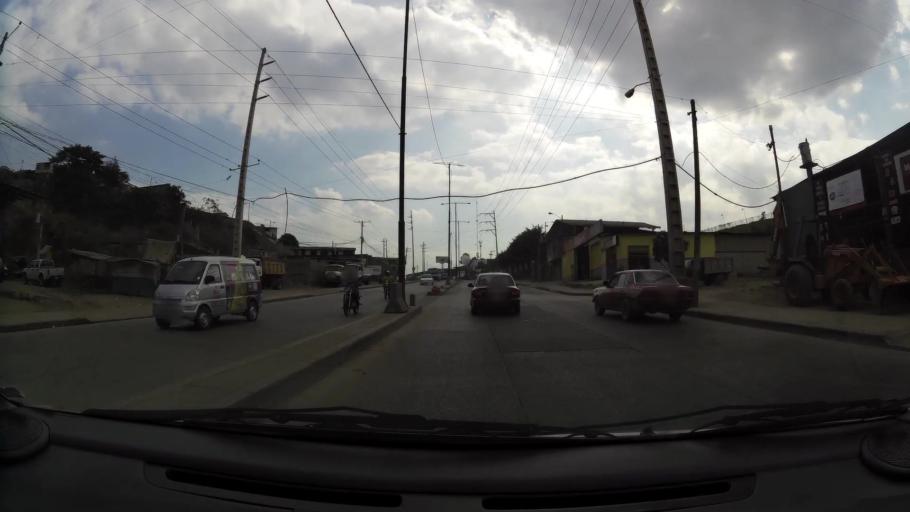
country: EC
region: Guayas
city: Santa Lucia
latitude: -2.1183
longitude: -79.9631
